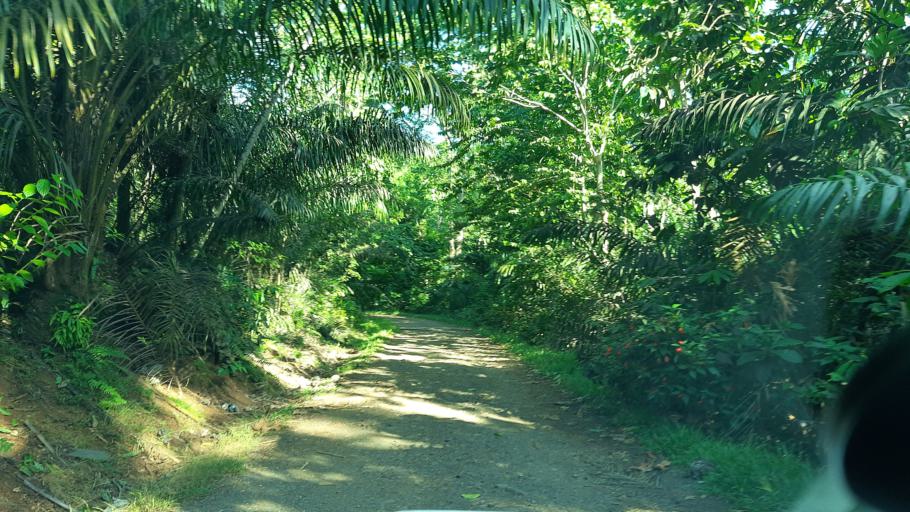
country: ST
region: Sao Tome Island
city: Sao Tome
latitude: 0.2446
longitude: 6.7395
